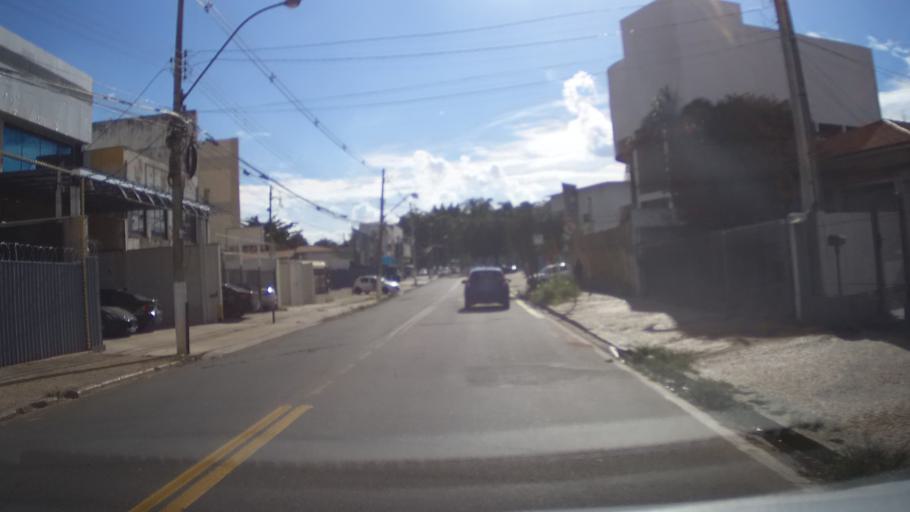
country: BR
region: Sao Paulo
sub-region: Campinas
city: Campinas
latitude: -22.8885
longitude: -47.0638
